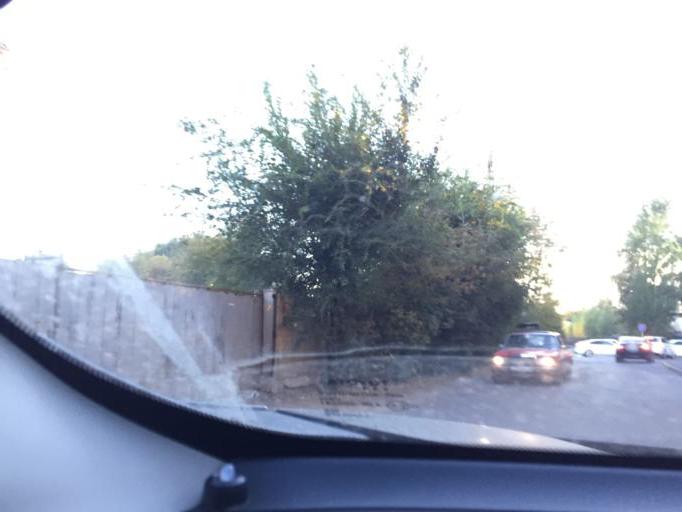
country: KZ
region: Astana Qalasy
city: Astana
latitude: 51.1462
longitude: 71.4259
